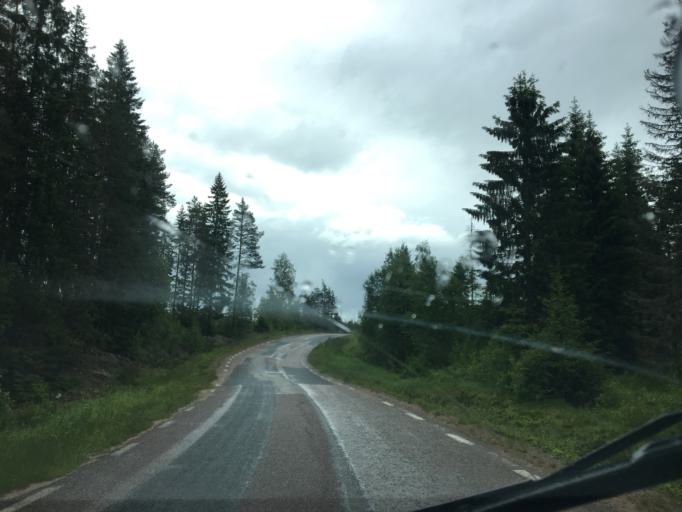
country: SE
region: OErebro
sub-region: Hallefors Kommun
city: Haellefors
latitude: 60.0759
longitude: 14.4864
